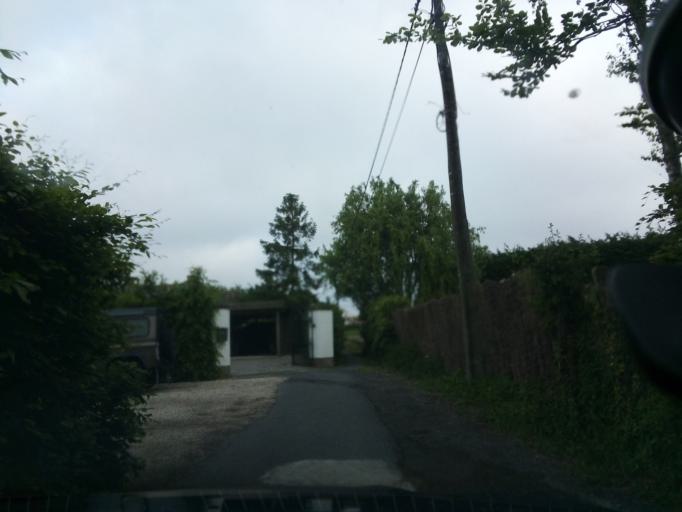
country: BE
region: Flanders
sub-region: Provincie West-Vlaanderen
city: Ingelmunster
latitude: 50.9421
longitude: 3.2403
